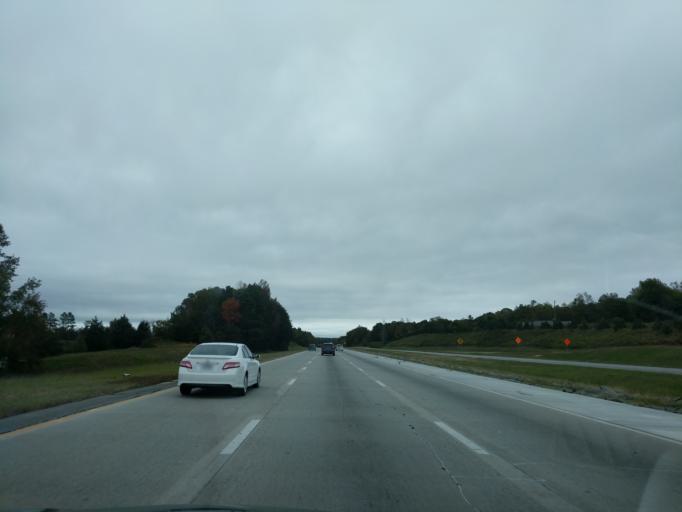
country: US
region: North Carolina
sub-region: Randolph County
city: Archdale
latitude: 35.9297
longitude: -79.9230
